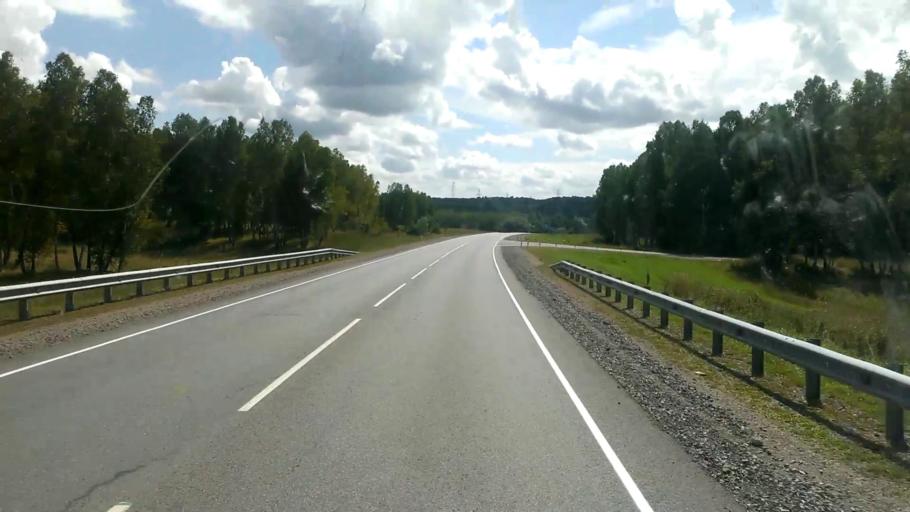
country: RU
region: Altai Krai
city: Troitskoye
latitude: 52.9394
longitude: 84.7838
